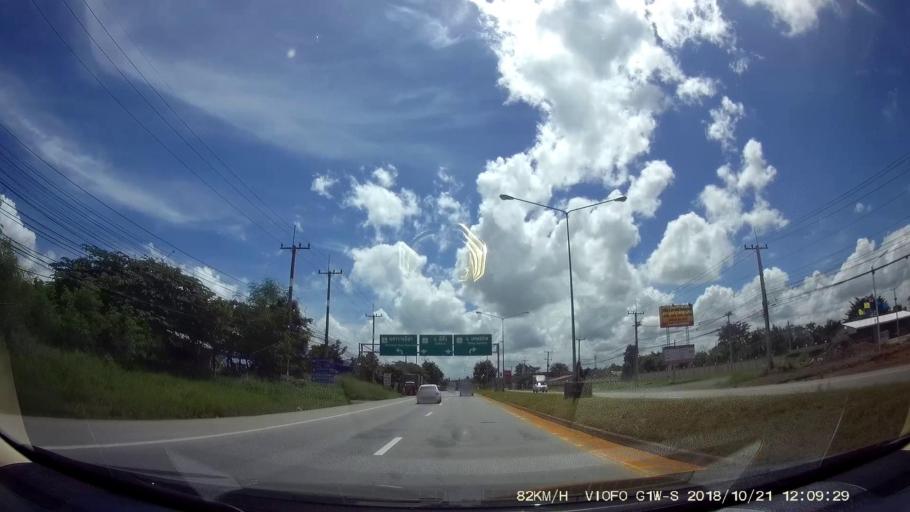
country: TH
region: Chaiyaphum
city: Chatturat
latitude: 15.4206
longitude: 101.8326
